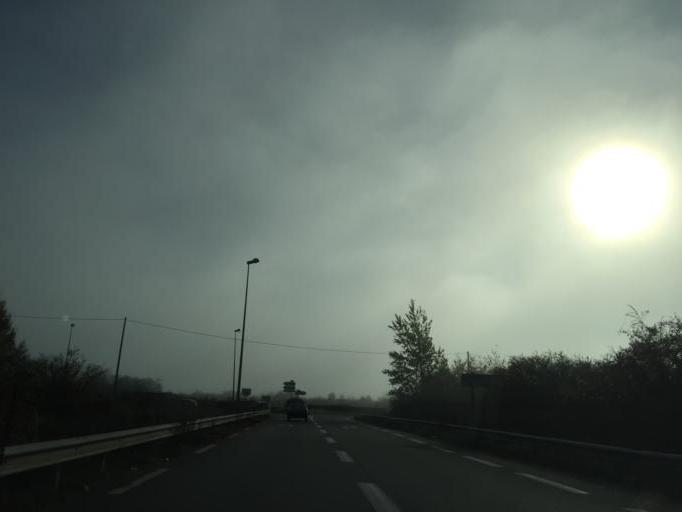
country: FR
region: Rhone-Alpes
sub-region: Departement du Rhone
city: Vourles
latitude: 45.6516
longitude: 4.7500
